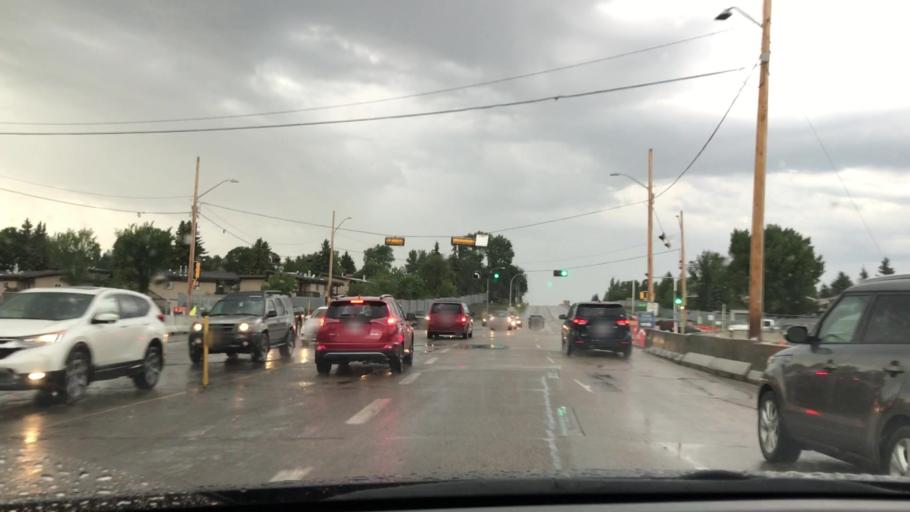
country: CA
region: Alberta
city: Edmonton
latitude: 53.4650
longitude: -113.4360
